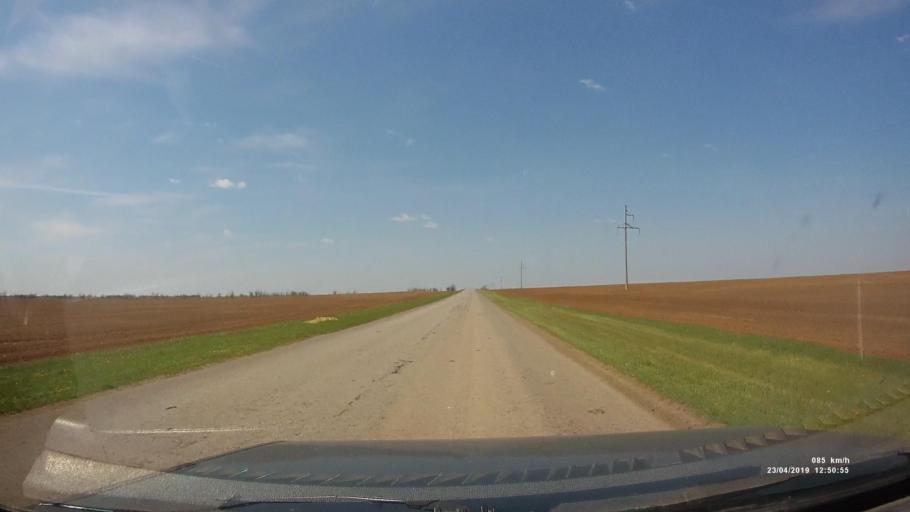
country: RU
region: Kalmykiya
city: Yashalta
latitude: 46.5499
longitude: 42.6296
